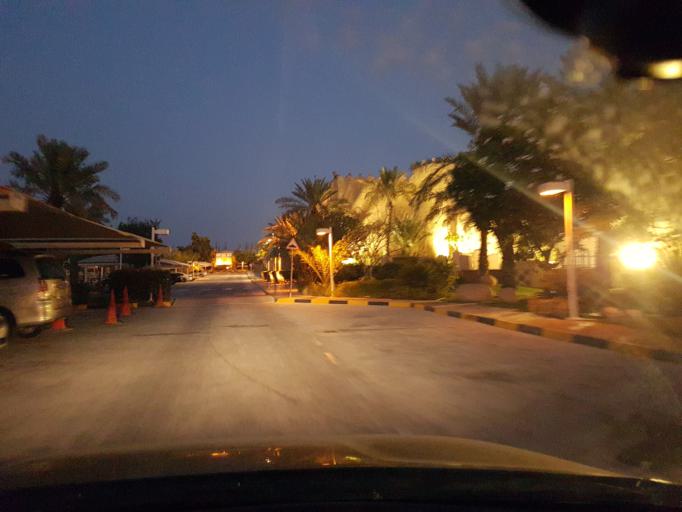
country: BH
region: Central Governorate
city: Dar Kulayb
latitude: 26.0147
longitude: 50.5091
